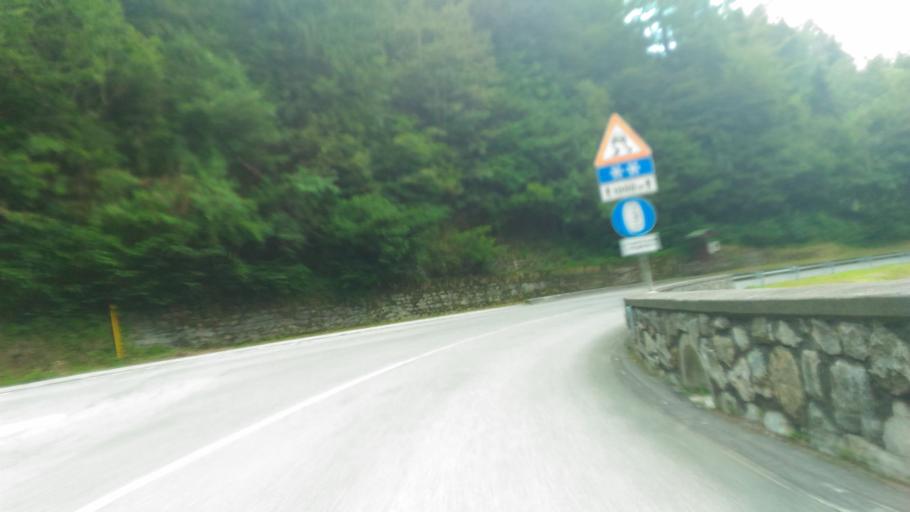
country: IT
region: Lombardy
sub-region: Provincia di Bergamo
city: Piazzolo
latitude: 45.9893
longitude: 9.6731
